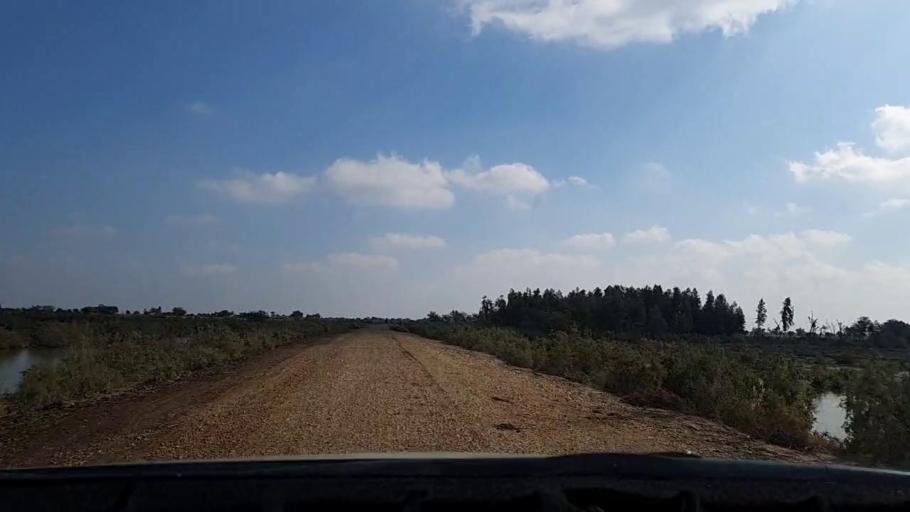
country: PK
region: Sindh
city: Pithoro
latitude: 25.7310
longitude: 69.2852
